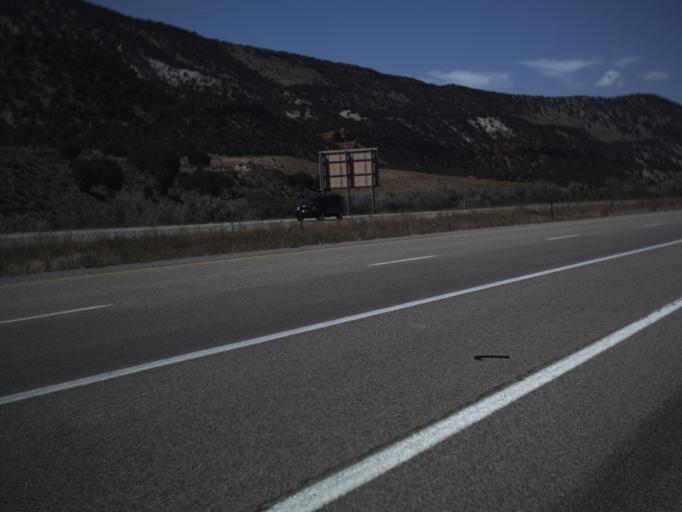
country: US
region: Utah
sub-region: Sevier County
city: Salina
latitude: 38.9179
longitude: -111.7469
